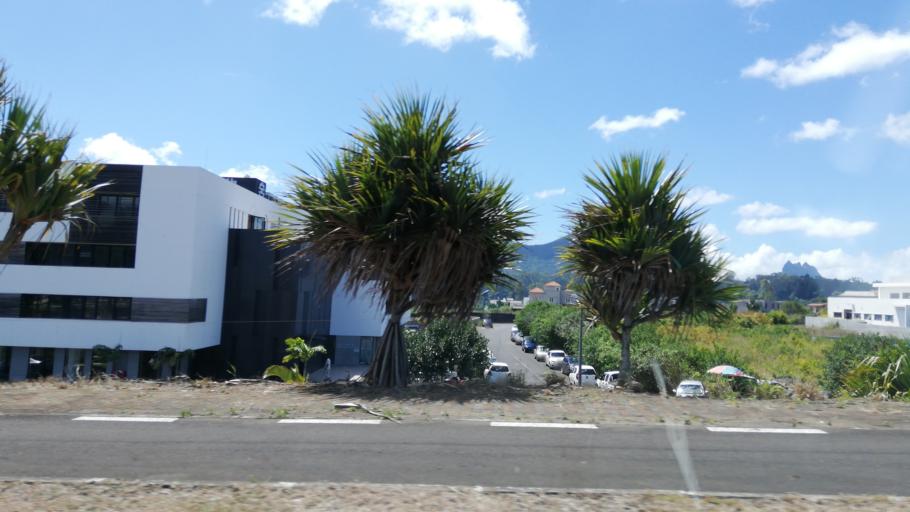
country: MU
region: Plaines Wilhems
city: Ebene
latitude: -20.2405
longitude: 57.4852
